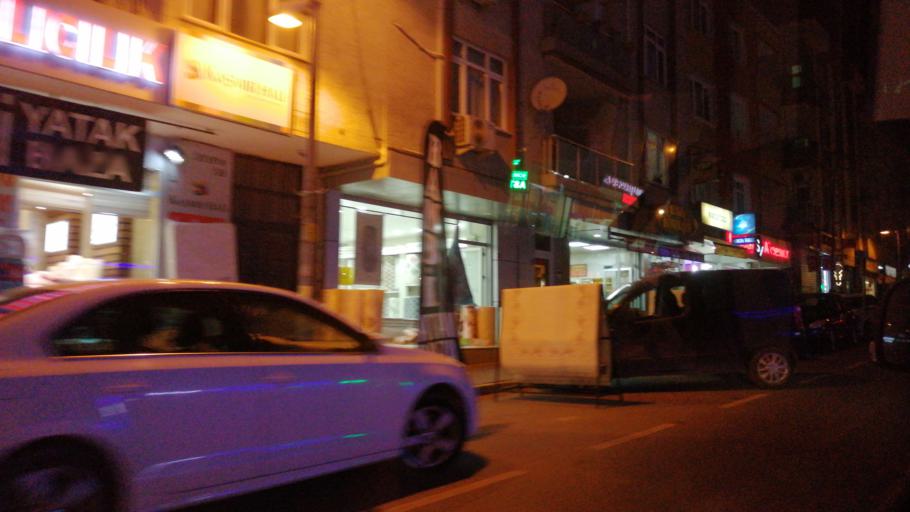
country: TR
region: Istanbul
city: Umraniye
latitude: 41.0117
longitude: 29.1280
